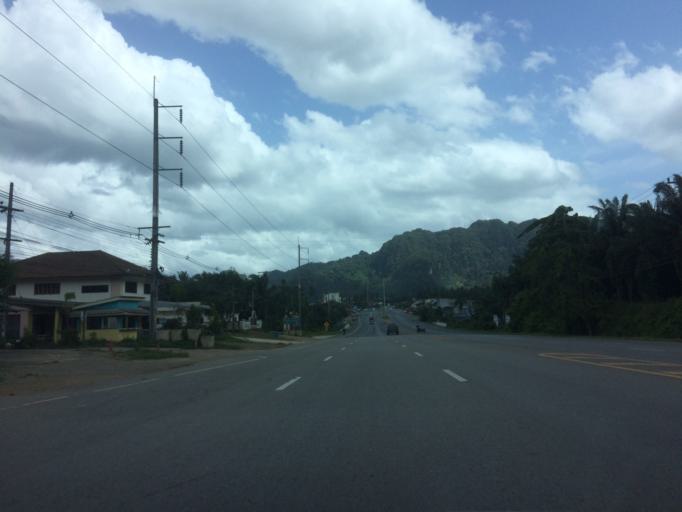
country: TH
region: Phangnga
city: Ban Ao Nang
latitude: 8.2206
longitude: 98.8086
